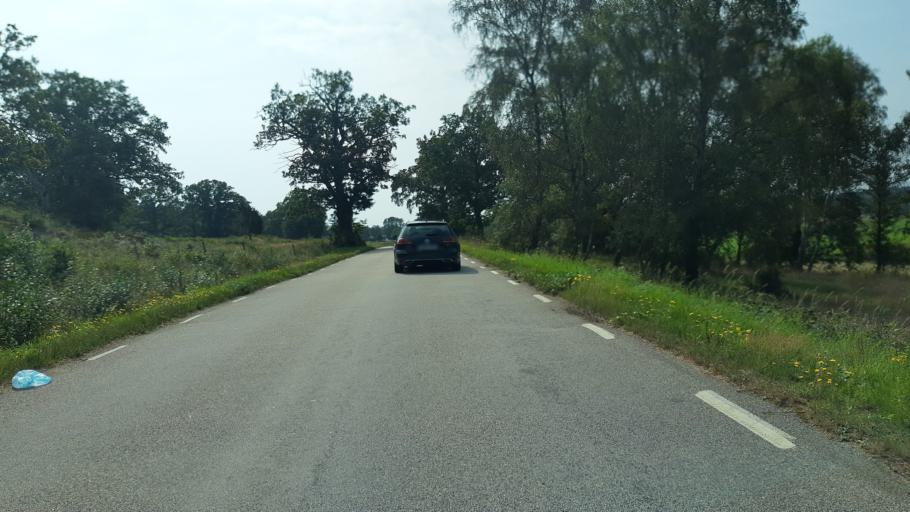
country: SE
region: Blekinge
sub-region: Ronneby Kommun
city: Kallinge
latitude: 56.2153
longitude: 15.3549
